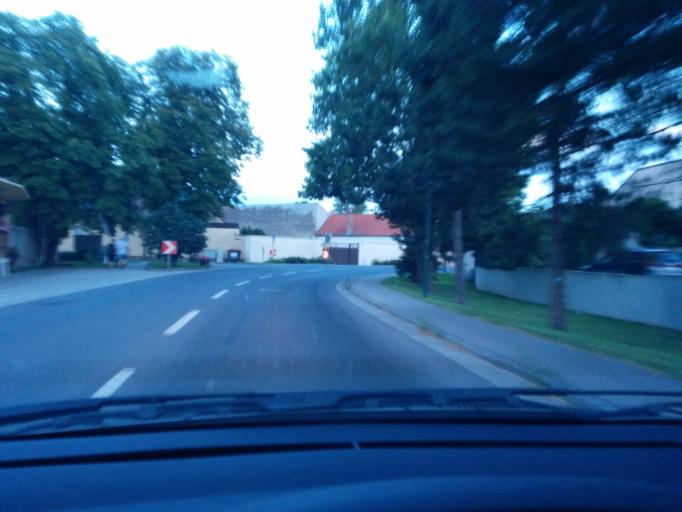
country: AT
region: Lower Austria
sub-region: Politischer Bezirk Modling
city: Munchendorf
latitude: 48.0328
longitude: 16.3811
